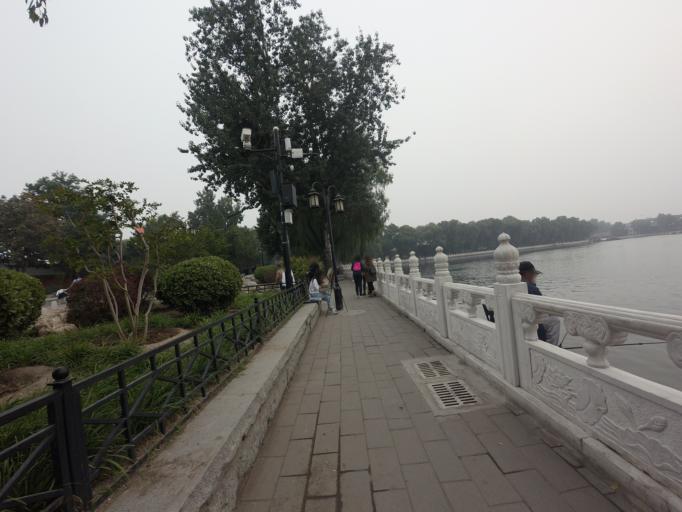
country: CN
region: Beijing
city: Jingshan
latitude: 39.9358
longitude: 116.3887
